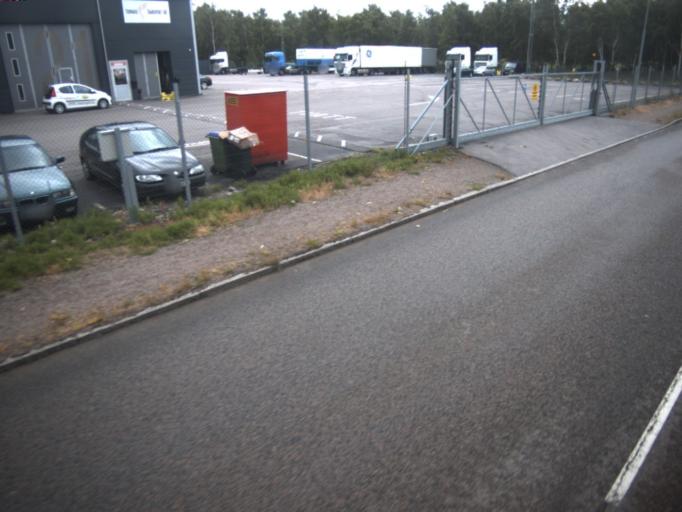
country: SE
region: Skane
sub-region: Helsingborg
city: Helsingborg
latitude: 56.0114
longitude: 12.7197
